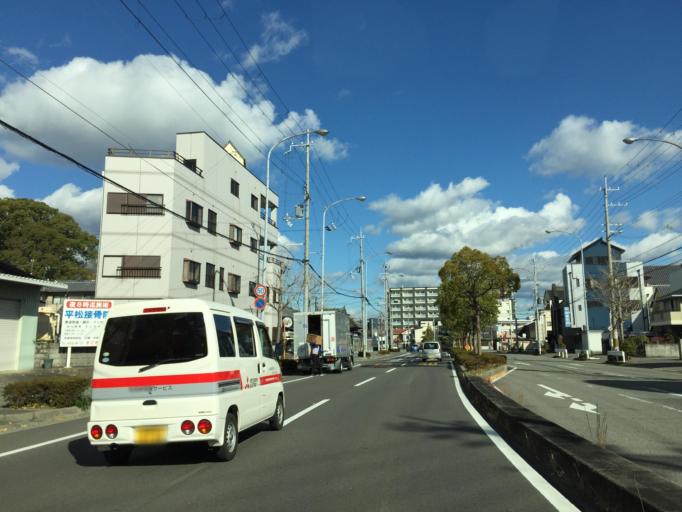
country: JP
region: Wakayama
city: Wakayama-shi
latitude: 34.2158
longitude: 135.1778
